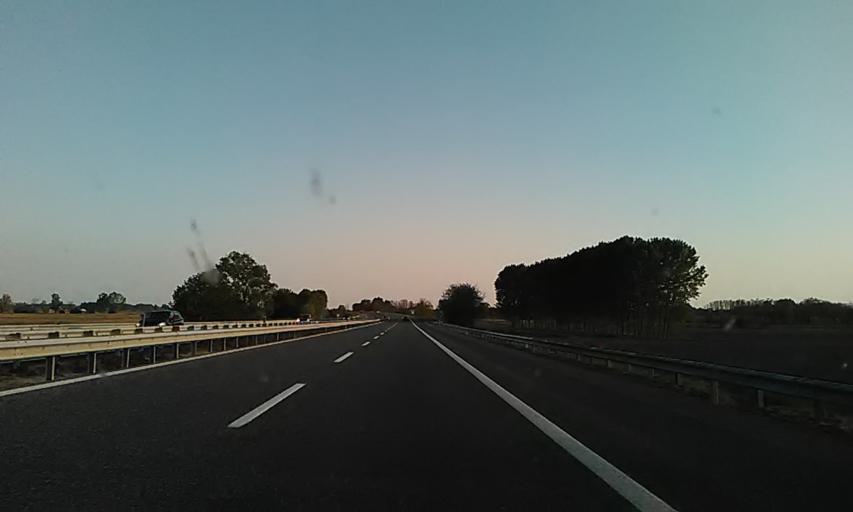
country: IT
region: Piedmont
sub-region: Provincia di Novara
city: Sillavengo
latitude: 45.5168
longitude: 8.4321
